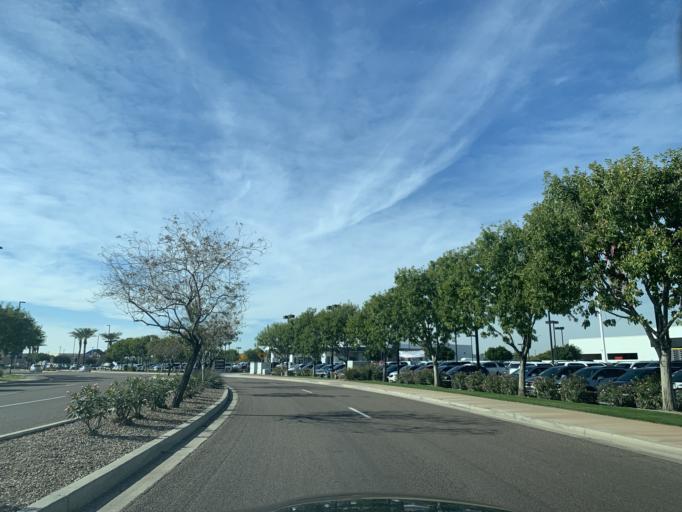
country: US
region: Arizona
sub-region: Maricopa County
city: Gilbert
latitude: 33.2923
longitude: -111.7562
